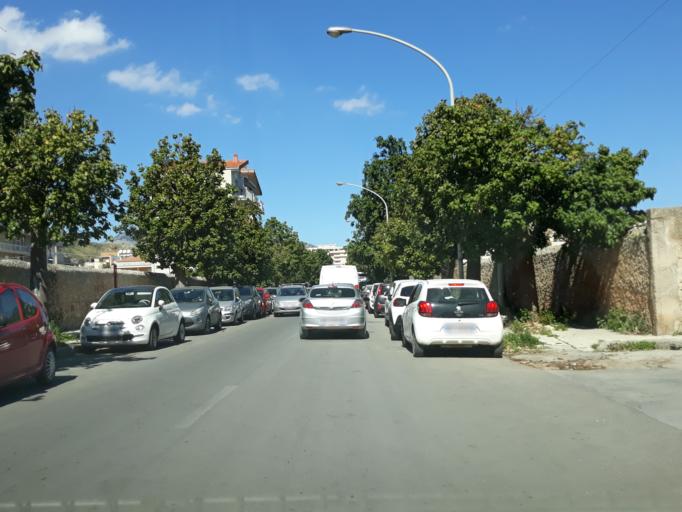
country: IT
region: Sicily
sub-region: Palermo
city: Monreale
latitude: 38.0931
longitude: 13.3201
